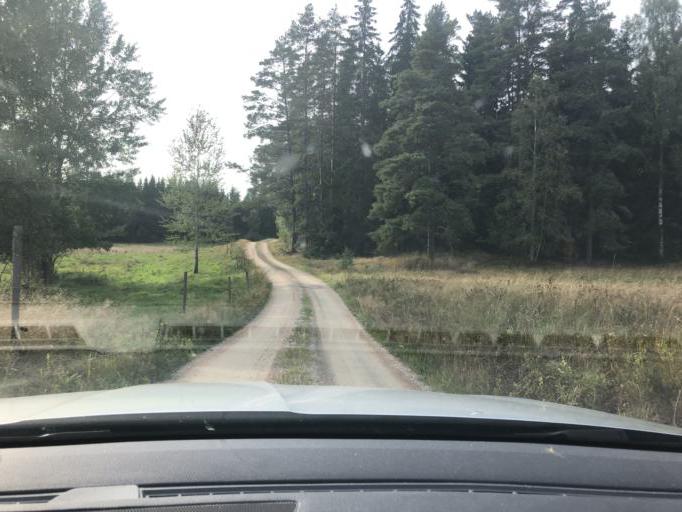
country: SE
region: Joenkoeping
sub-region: Vetlanda Kommun
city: Ekenassjon
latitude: 57.4989
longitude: 14.9036
